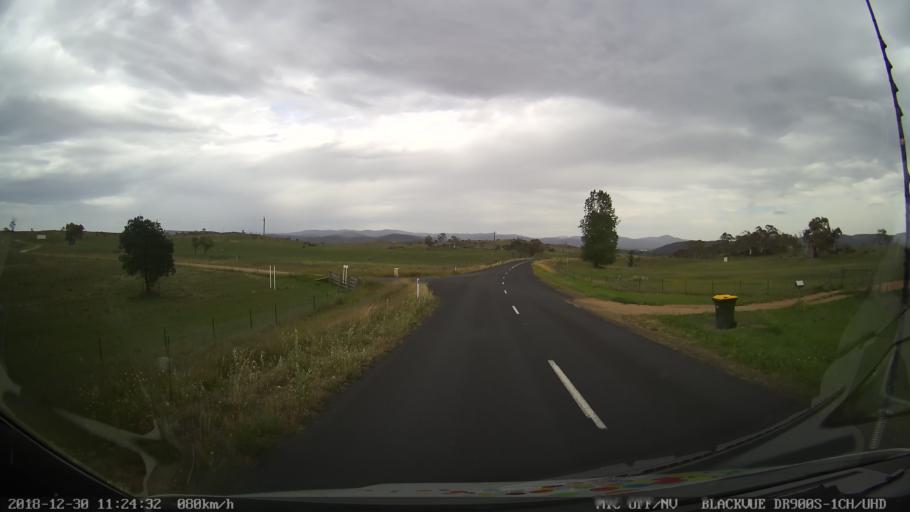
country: AU
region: New South Wales
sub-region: Snowy River
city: Jindabyne
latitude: -36.4824
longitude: 148.6493
